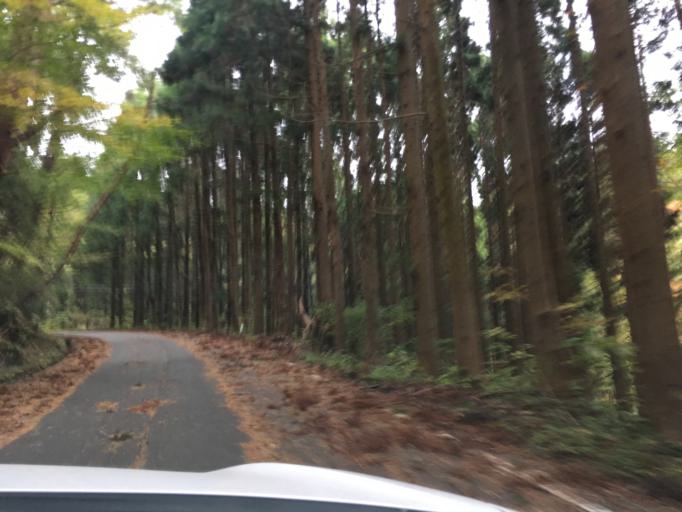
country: JP
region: Fukushima
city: Iwaki
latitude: 37.0988
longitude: 140.8003
